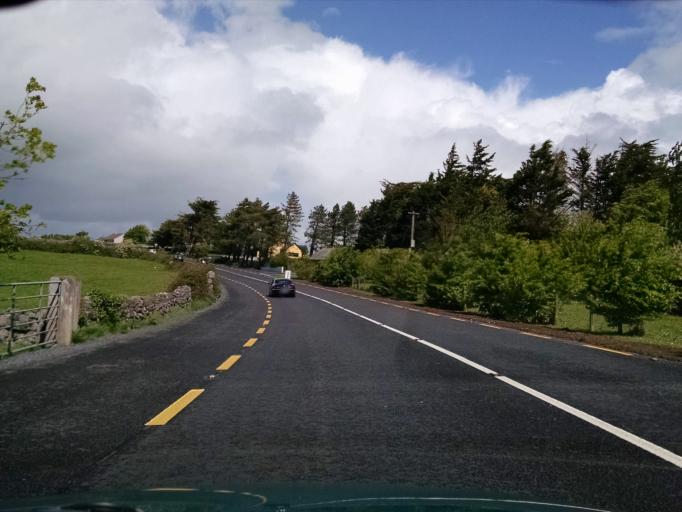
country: IE
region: Connaught
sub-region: County Galway
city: Oranmore
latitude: 53.2356
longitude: -8.8820
